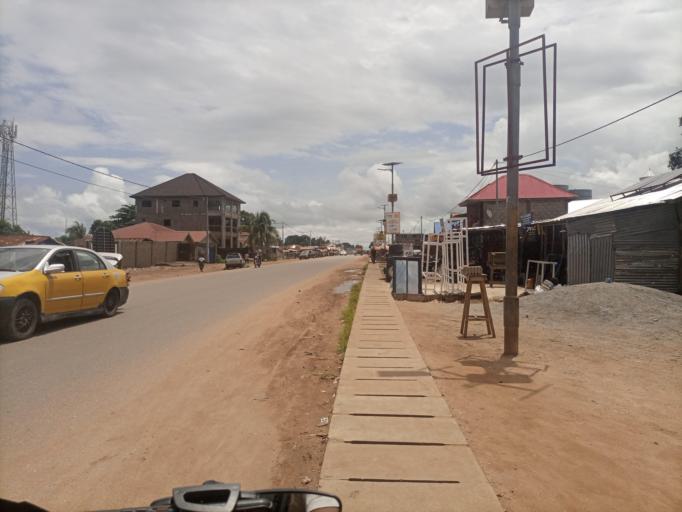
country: SL
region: Northern Province
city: Masoyila
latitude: 8.6029
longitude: -13.1782
